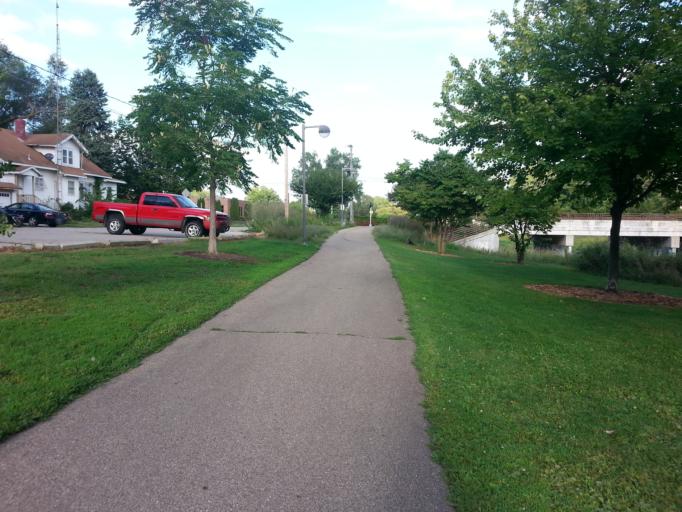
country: US
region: Minnesota
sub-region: Olmsted County
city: Rochester
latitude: 44.0263
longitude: -92.4798
